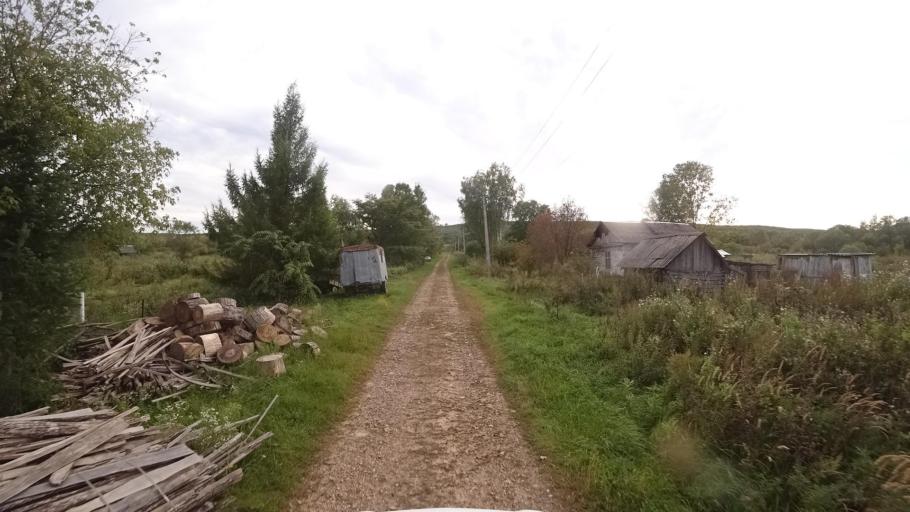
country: RU
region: Primorskiy
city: Dostoyevka
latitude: 44.3474
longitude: 133.4089
